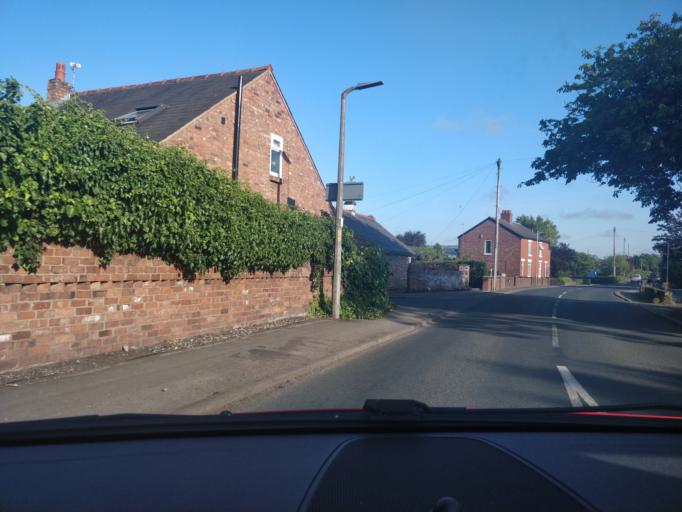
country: GB
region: England
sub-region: Lancashire
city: Banks
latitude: 53.6624
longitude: -2.8798
